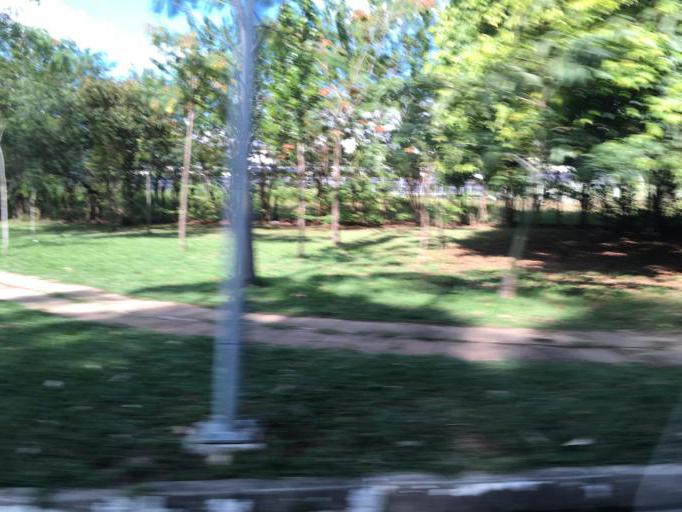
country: BR
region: Sao Paulo
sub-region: Osasco
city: Osasco
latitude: -23.5574
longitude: -46.7349
